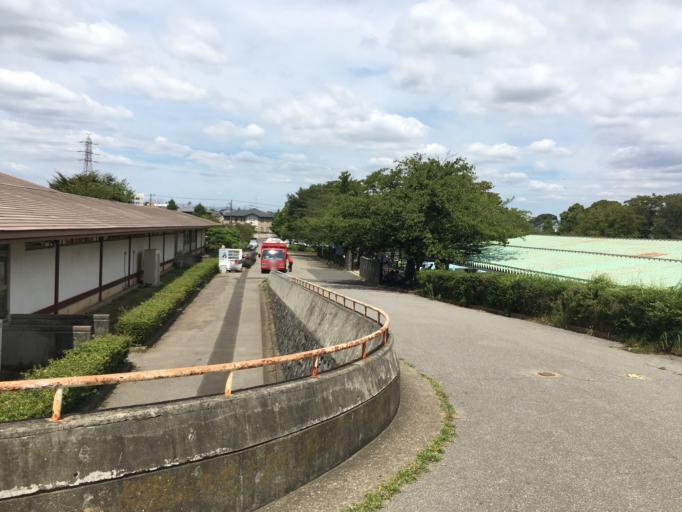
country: JP
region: Chiba
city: Matsudo
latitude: 35.7965
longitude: 139.9260
